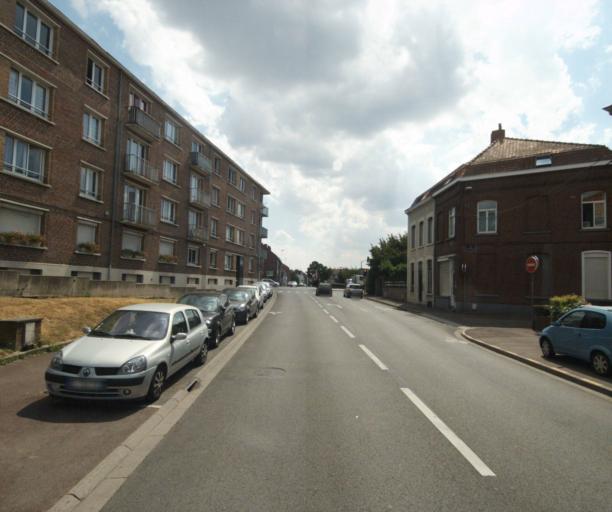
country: FR
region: Nord-Pas-de-Calais
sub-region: Departement du Nord
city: Neuville-en-Ferrain
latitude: 50.7387
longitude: 3.1624
